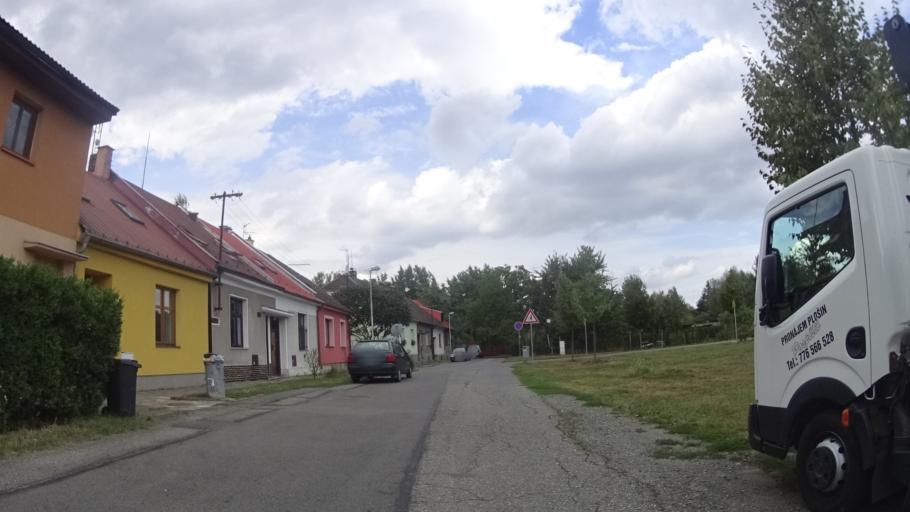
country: CZ
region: Olomoucky
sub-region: Okres Olomouc
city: Olomouc
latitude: 49.6100
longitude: 17.2348
